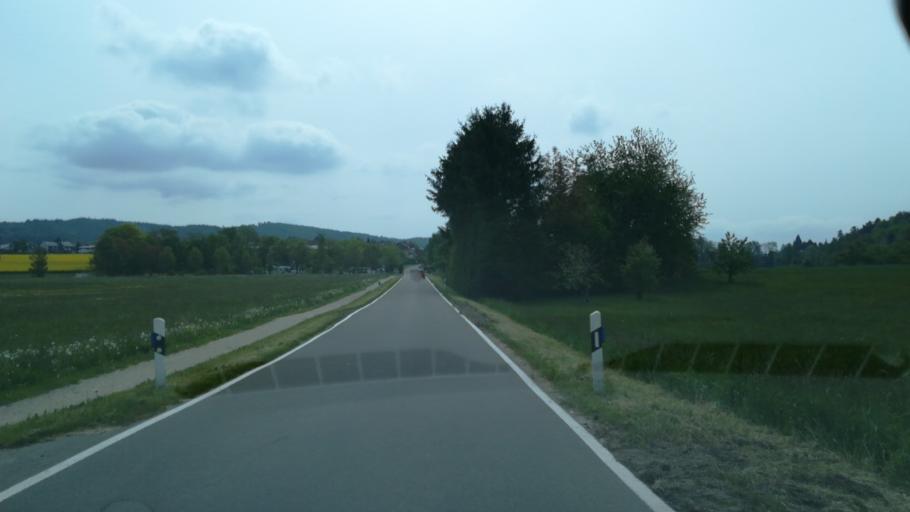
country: DE
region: Baden-Wuerttemberg
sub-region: Freiburg Region
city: Steisslingen
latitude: 47.8025
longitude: 8.9121
